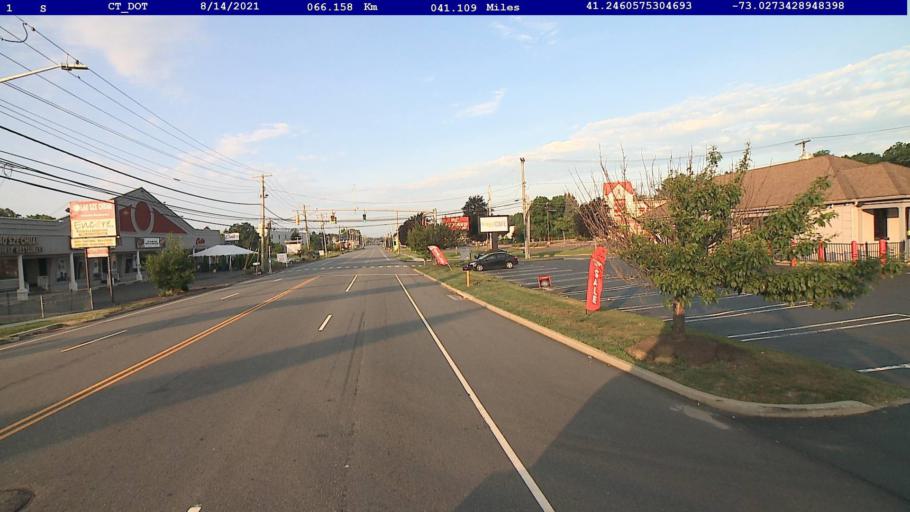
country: US
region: Connecticut
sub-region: New Haven County
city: Orange
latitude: 41.2461
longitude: -73.0274
